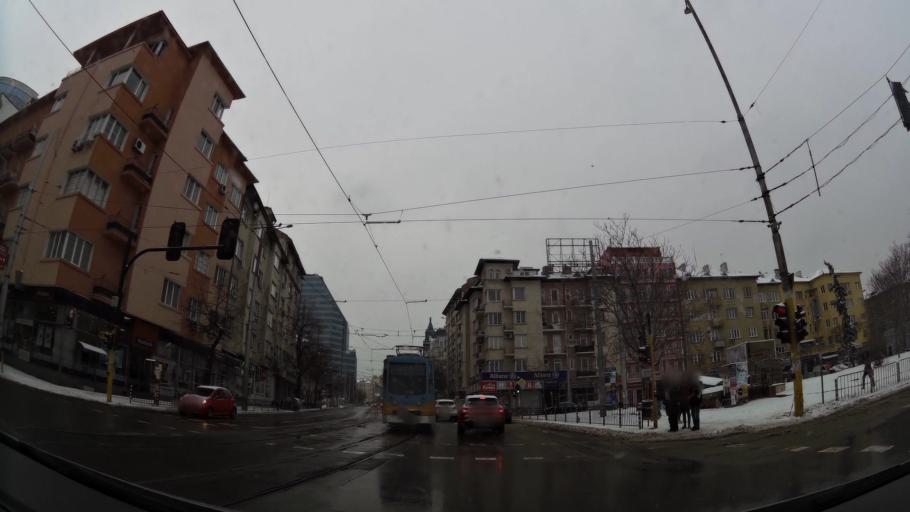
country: BG
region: Sofia-Capital
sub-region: Stolichna Obshtina
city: Sofia
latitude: 42.6977
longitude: 23.3152
